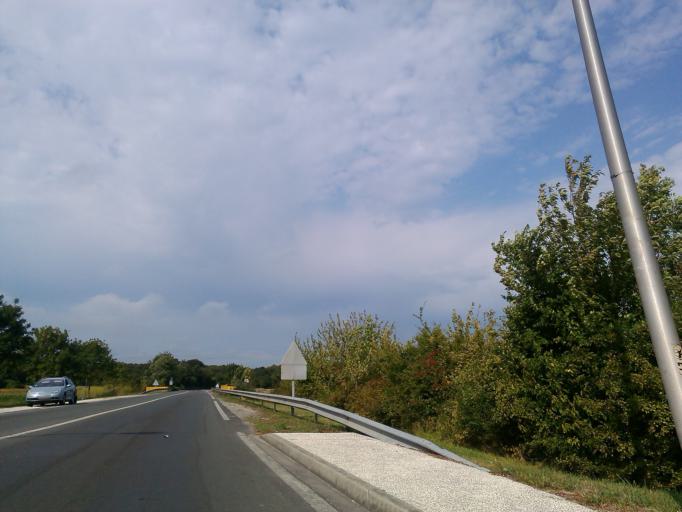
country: FR
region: Poitou-Charentes
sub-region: Departement de la Charente-Maritime
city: La Tremblade
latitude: 45.7564
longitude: -1.1487
